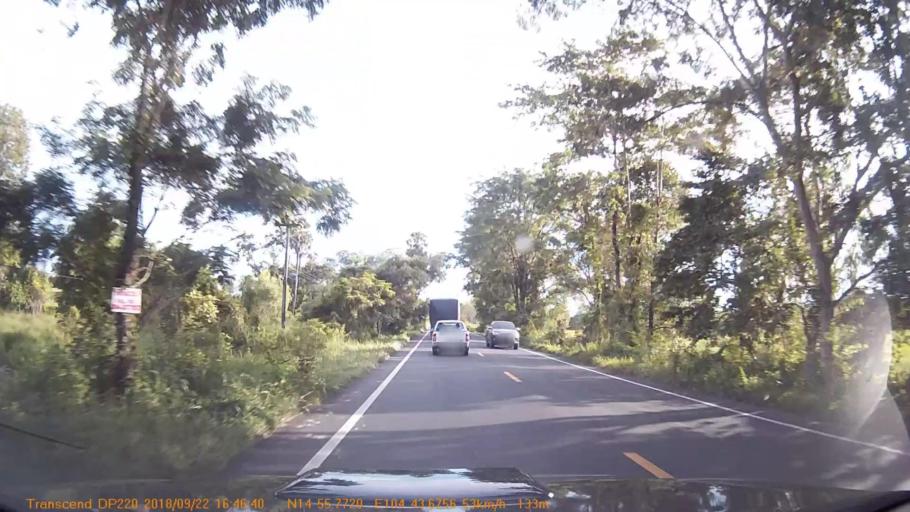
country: TH
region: Sisaket
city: Non Kho
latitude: 14.9294
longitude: 104.7279
